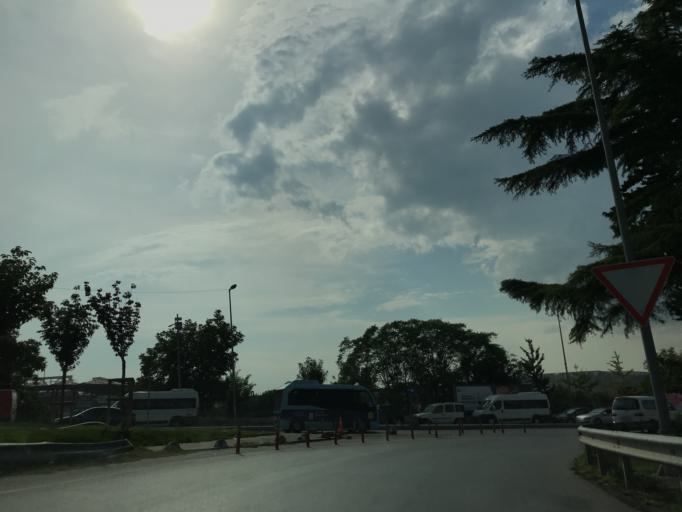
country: TR
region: Istanbul
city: UEskuedar
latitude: 40.9908
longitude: 29.0404
